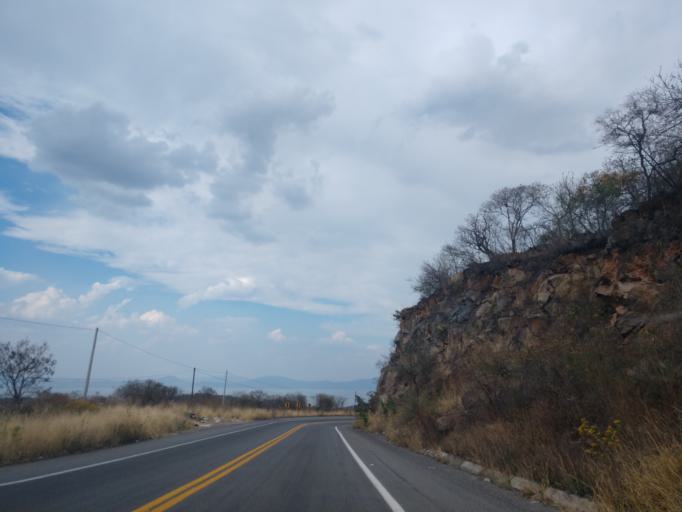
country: MX
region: Jalisco
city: La Manzanilla de la Paz
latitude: 20.1030
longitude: -103.1708
